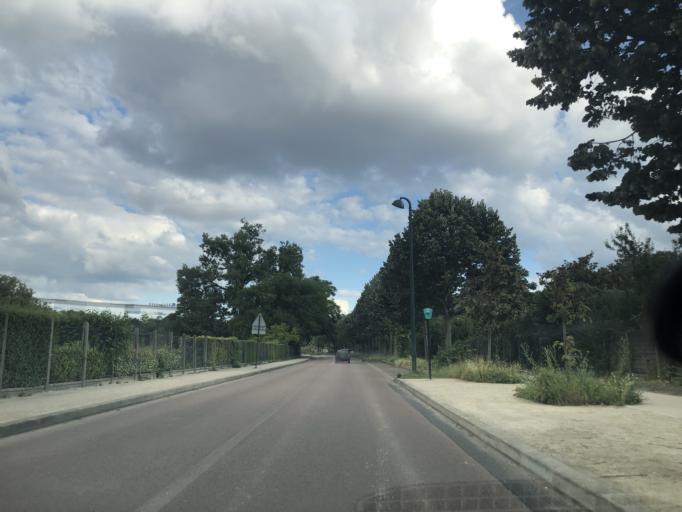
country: FR
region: Ile-de-France
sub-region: Departement du Val-de-Marne
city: Joinville-le-Pont
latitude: 48.8224
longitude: 2.4590
